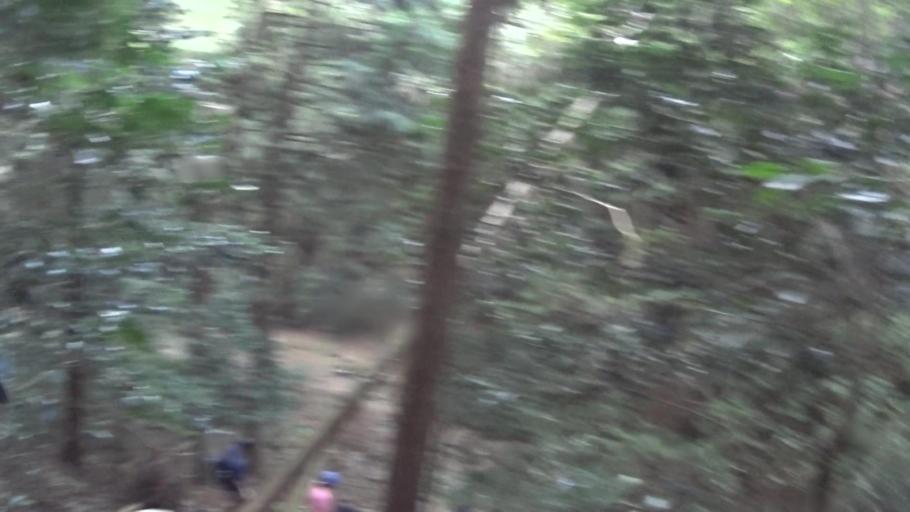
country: JP
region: Osaka
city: Kaizuka
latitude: 34.4821
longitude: 135.3147
